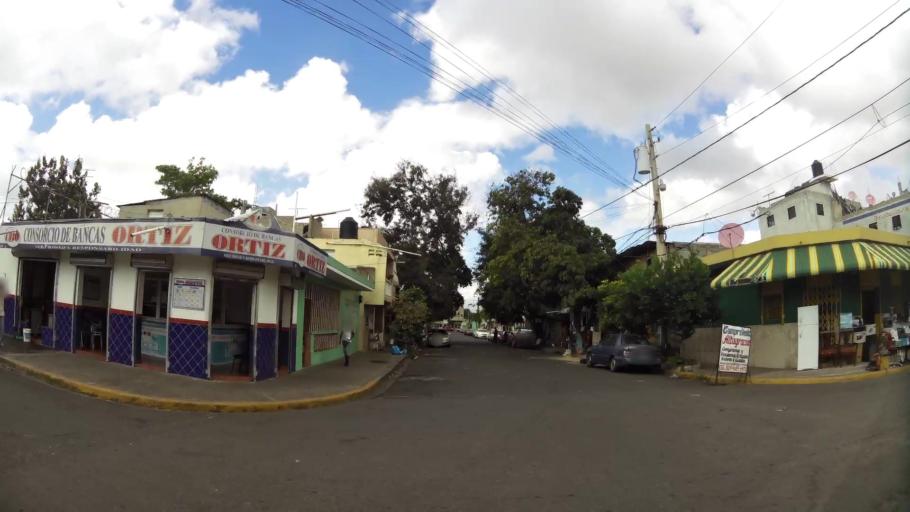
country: DO
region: Nacional
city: San Carlos
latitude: 18.4848
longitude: -69.8969
